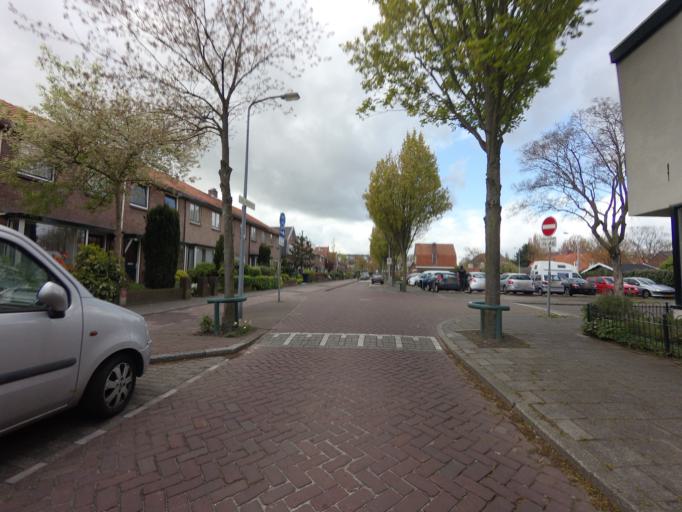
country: NL
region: Utrecht
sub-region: Gemeente Zeist
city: Zeist
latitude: 52.0893
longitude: 5.2342
